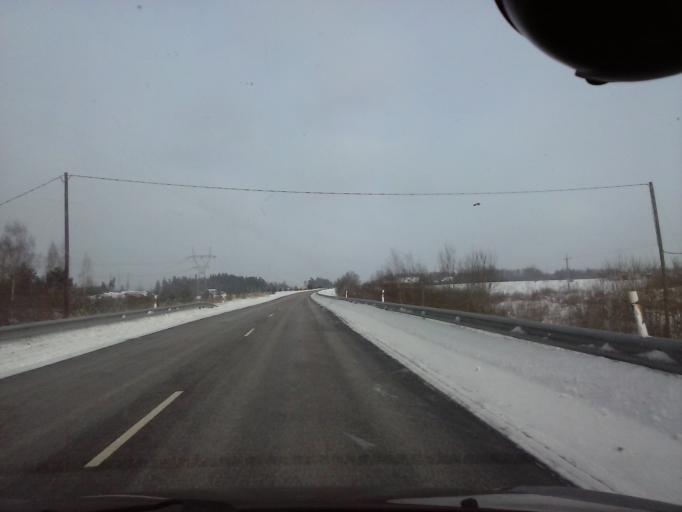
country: EE
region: Paernumaa
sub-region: Saarde vald
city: Kilingi-Nomme
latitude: 58.1630
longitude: 25.0120
